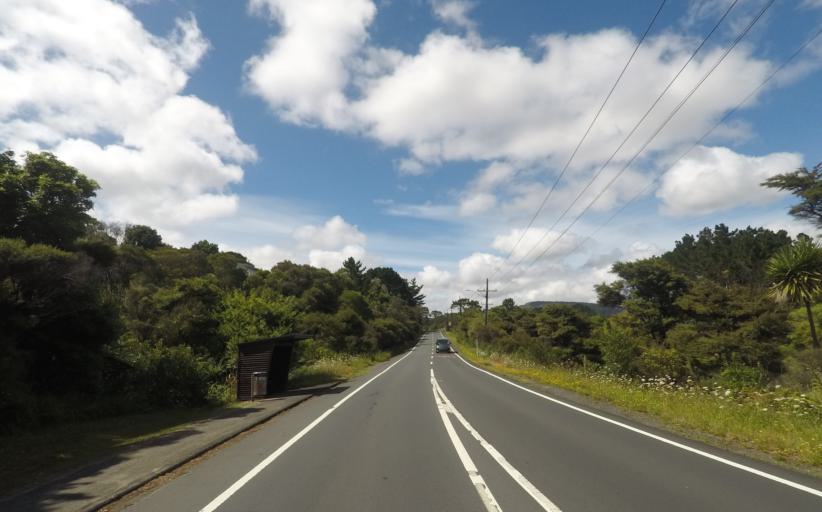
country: NZ
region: Auckland
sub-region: Auckland
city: Muriwai Beach
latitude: -36.8518
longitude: 174.5438
